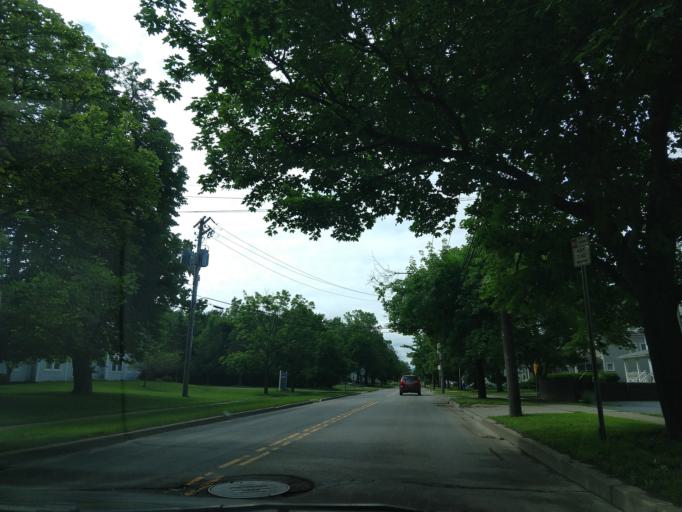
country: US
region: New York
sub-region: Erie County
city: East Aurora
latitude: 42.7654
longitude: -78.6079
